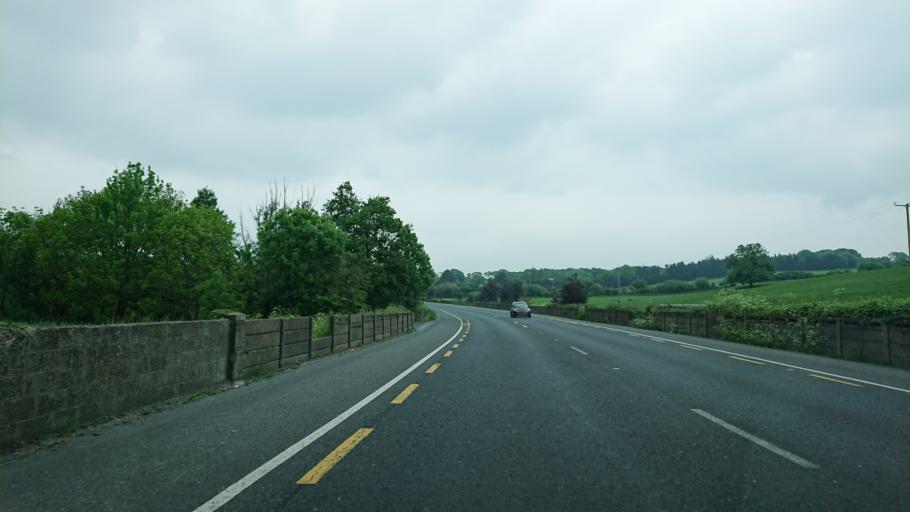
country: IE
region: Munster
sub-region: Waterford
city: Tra Mhor
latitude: 52.2022
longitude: -7.1170
